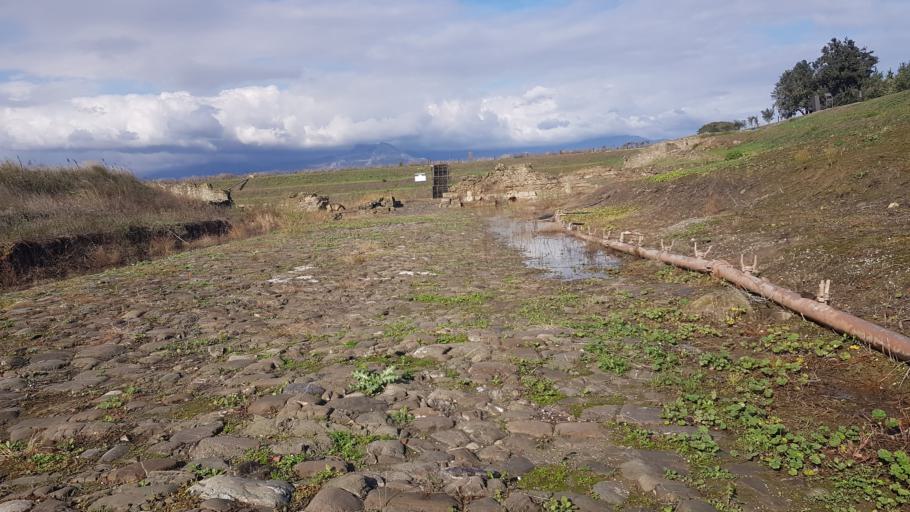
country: IT
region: Calabria
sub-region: Provincia di Cosenza
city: Sibari
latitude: 39.7180
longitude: 16.4892
